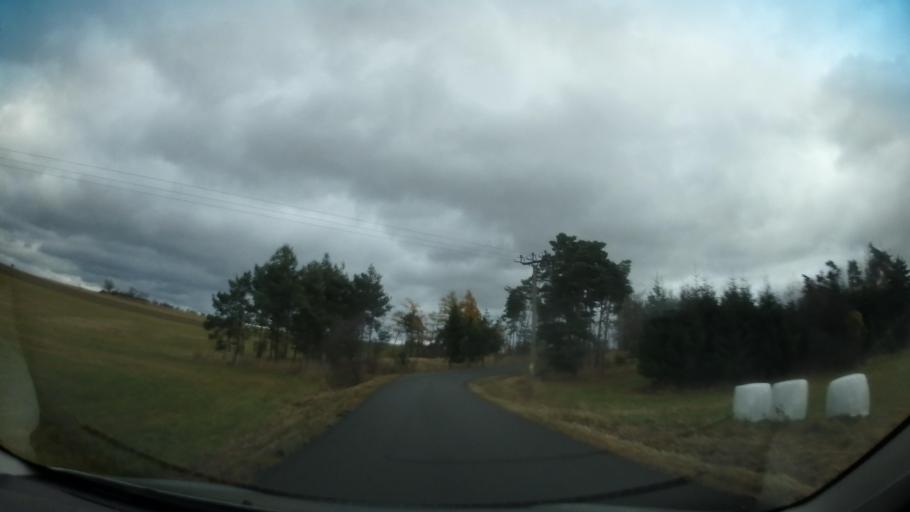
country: CZ
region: Vysocina
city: Namest' nad Oslavou
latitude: 49.2887
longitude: 16.1240
